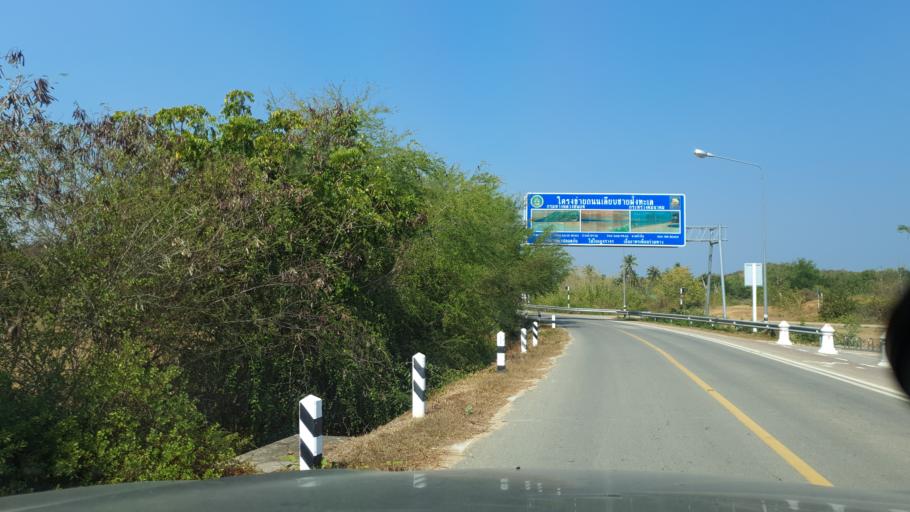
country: TH
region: Prachuap Khiri Khan
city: Sam Roi Yot
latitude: 12.2804
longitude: 99.9730
